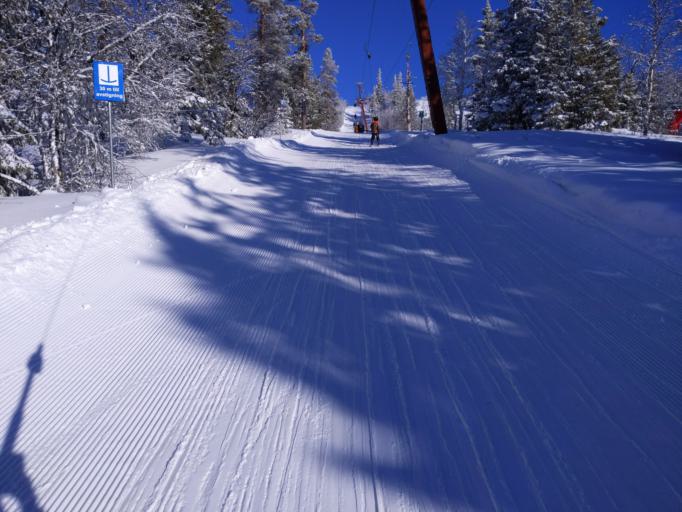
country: SE
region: Jaemtland
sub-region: Harjedalens Kommun
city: Sveg
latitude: 62.4311
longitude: 13.9598
